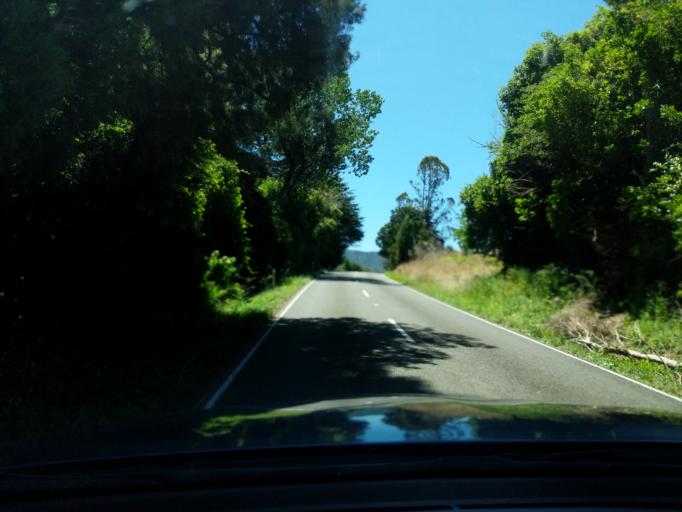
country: NZ
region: Tasman
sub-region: Tasman District
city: Takaka
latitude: -40.7621
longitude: 172.5635
